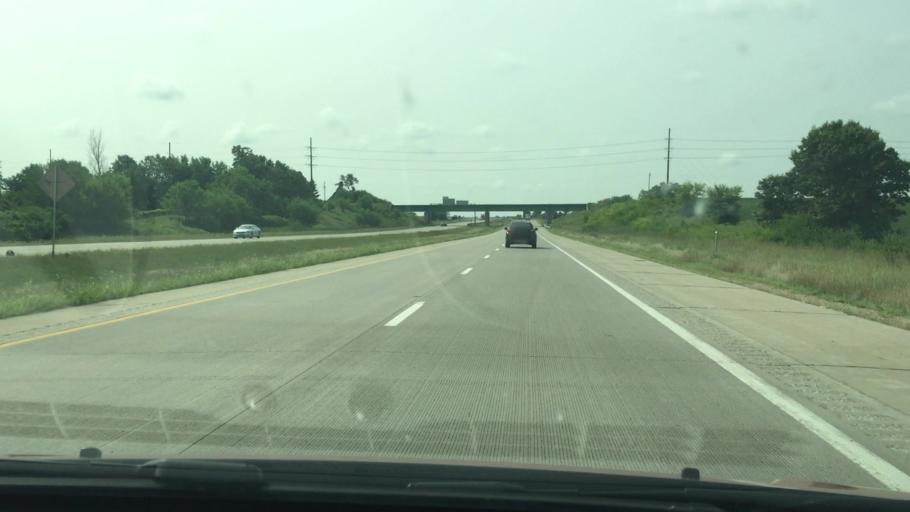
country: US
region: Iowa
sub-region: Scott County
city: Walcott
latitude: 41.5737
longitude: -90.6781
